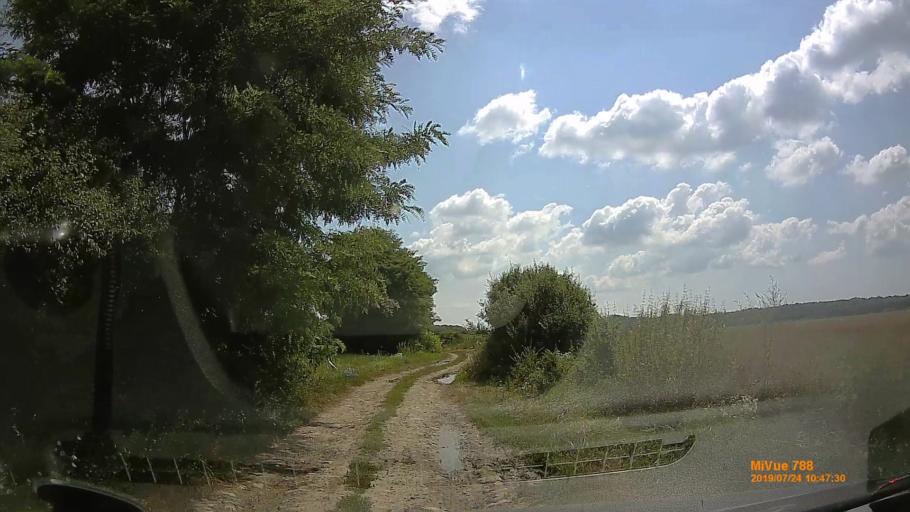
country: UA
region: Zakarpattia
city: Berehove
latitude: 48.1953
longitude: 22.5645
